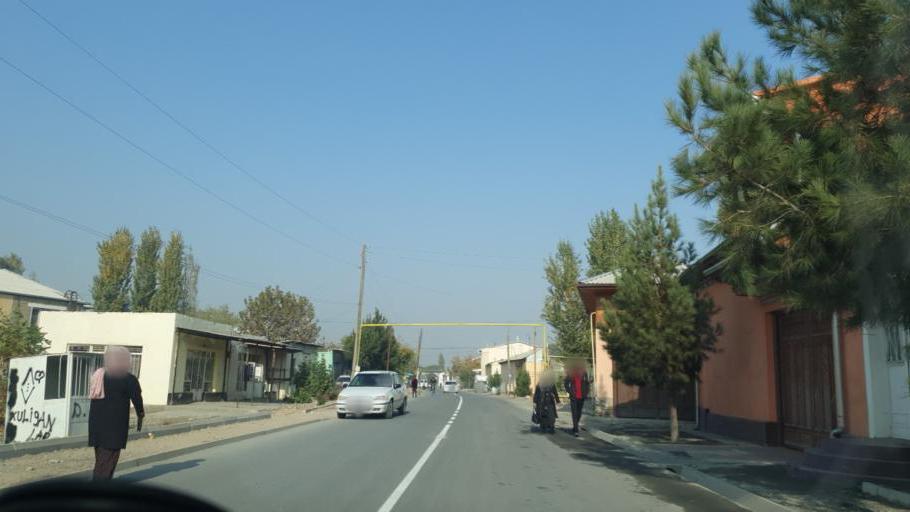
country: UZ
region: Fergana
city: Qo`qon
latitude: 40.5818
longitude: 70.9112
